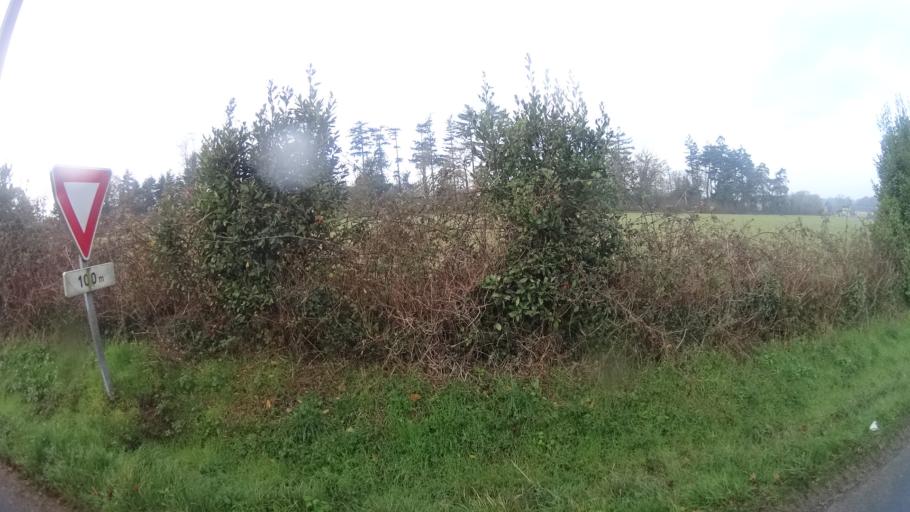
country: FR
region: Pays de la Loire
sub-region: Departement de la Loire-Atlantique
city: Avessac
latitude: 47.6513
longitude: -1.9939
